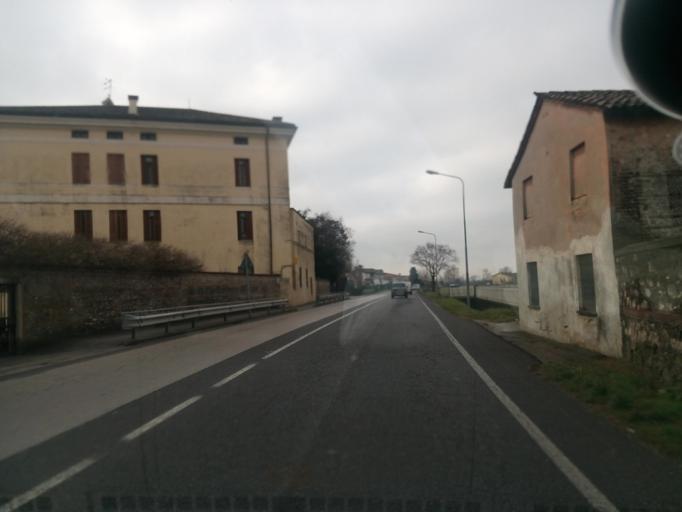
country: IT
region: Veneto
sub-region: Provincia di Vicenza
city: Bressanvido
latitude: 45.6636
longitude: 11.6346
